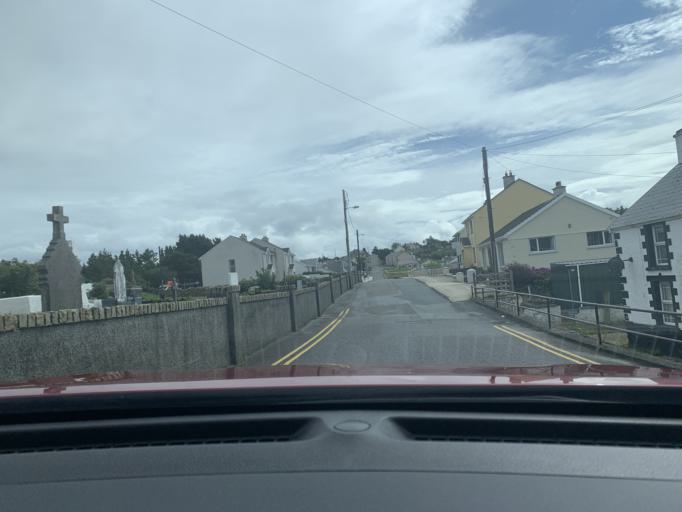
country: IE
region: Ulster
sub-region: County Donegal
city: Dungloe
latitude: 54.9479
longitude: -8.3596
